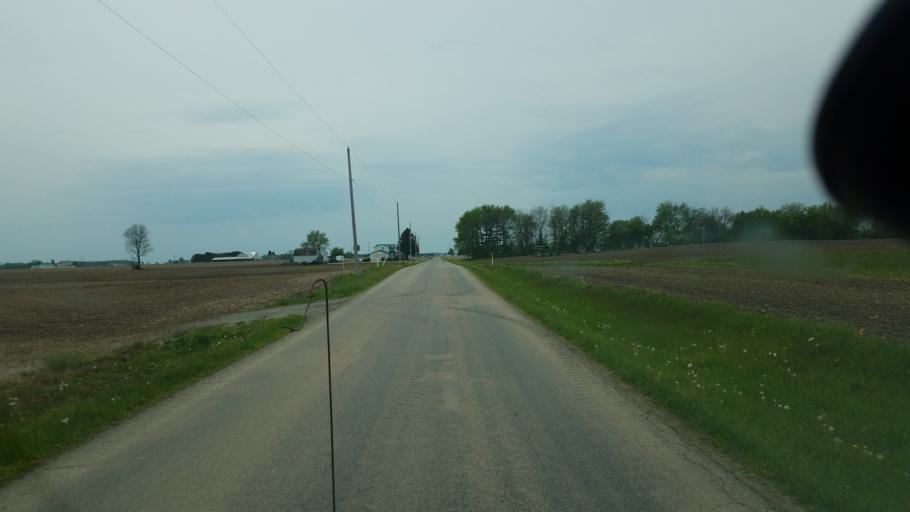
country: US
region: Ohio
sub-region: Richland County
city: Shelby
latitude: 40.8951
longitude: -82.6752
